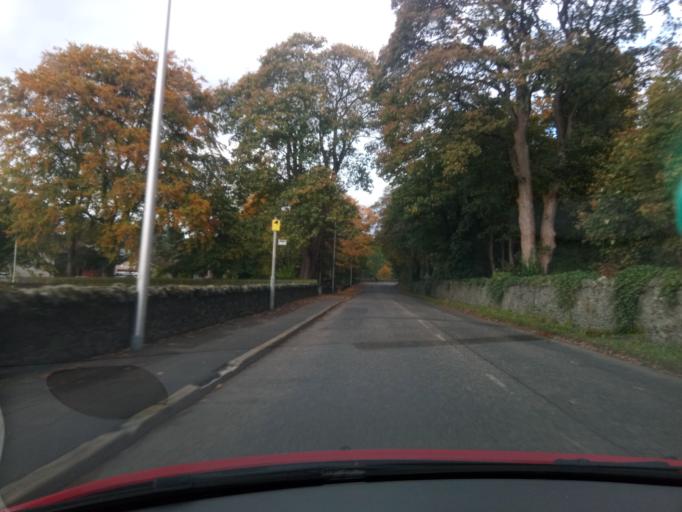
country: GB
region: Scotland
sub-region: The Scottish Borders
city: Peebles
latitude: 55.6476
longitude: -3.1821
